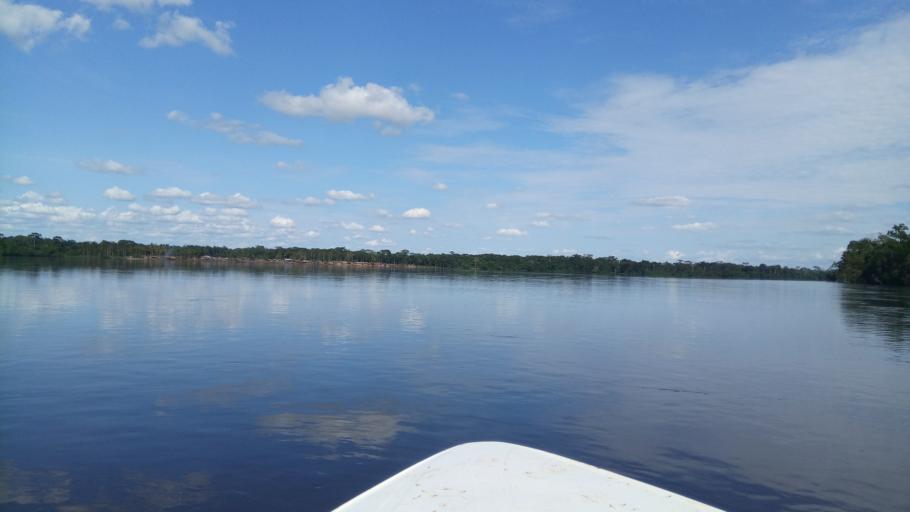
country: CD
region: Eastern Province
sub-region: Sous-Region de la Tshopo
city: Yangambi
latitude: 0.5522
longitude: 24.2418
